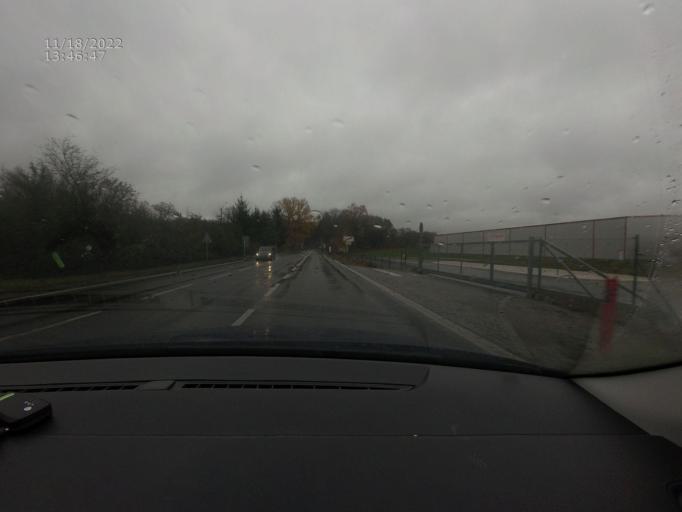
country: CZ
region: Jihocesky
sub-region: Okres Strakonice
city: Blatna
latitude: 49.4245
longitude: 13.8664
